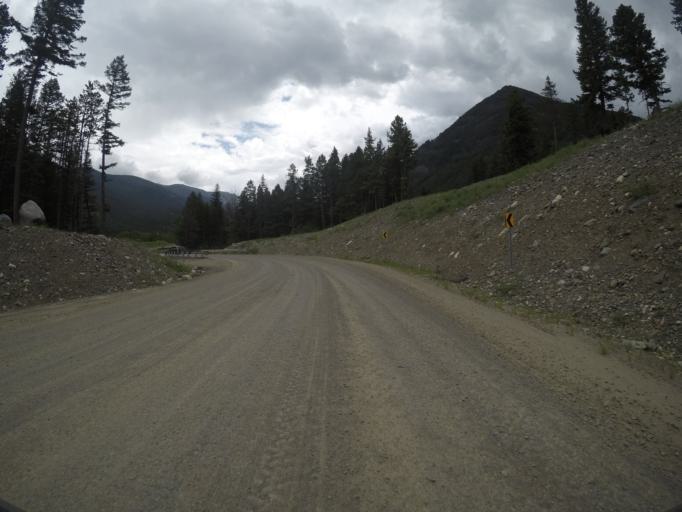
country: US
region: Montana
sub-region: Park County
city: Livingston
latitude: 45.4879
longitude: -110.2177
